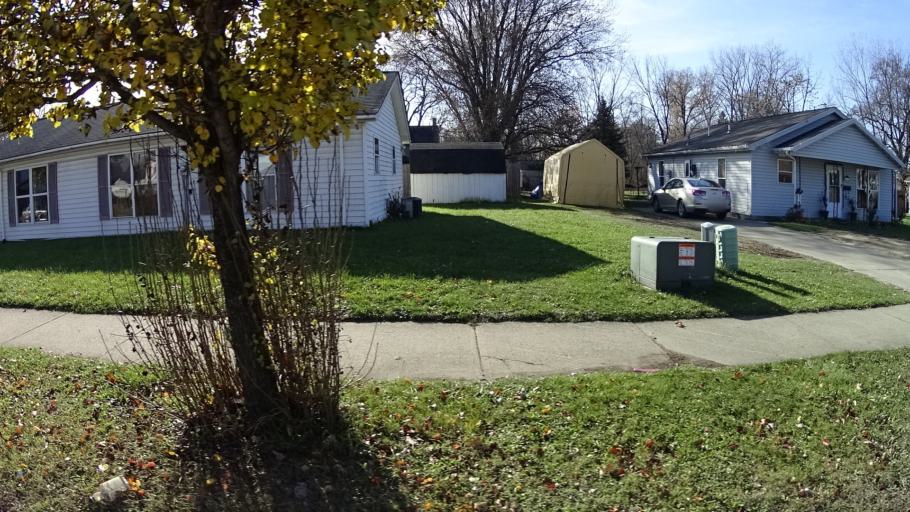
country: US
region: Ohio
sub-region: Lorain County
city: Elyria
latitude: 41.3729
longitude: -82.1142
